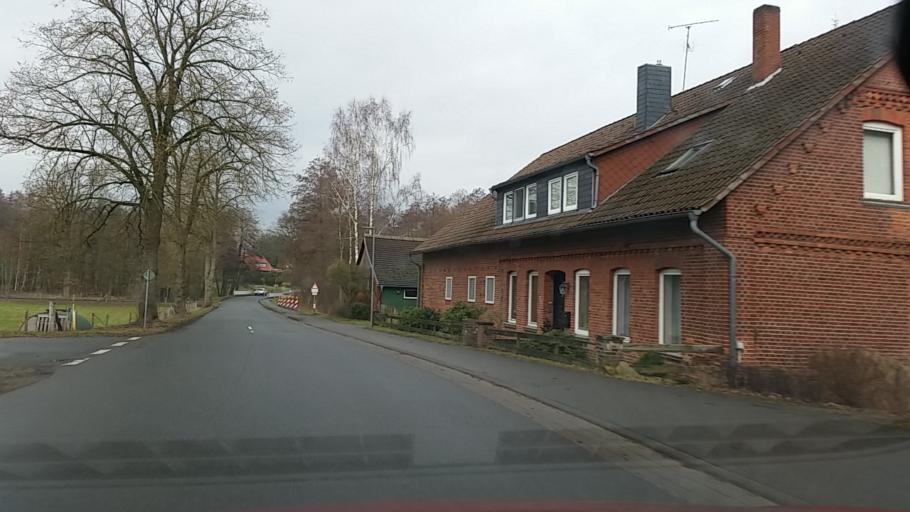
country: DE
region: Lower Saxony
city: Bispingen
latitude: 53.1023
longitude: 10.0045
